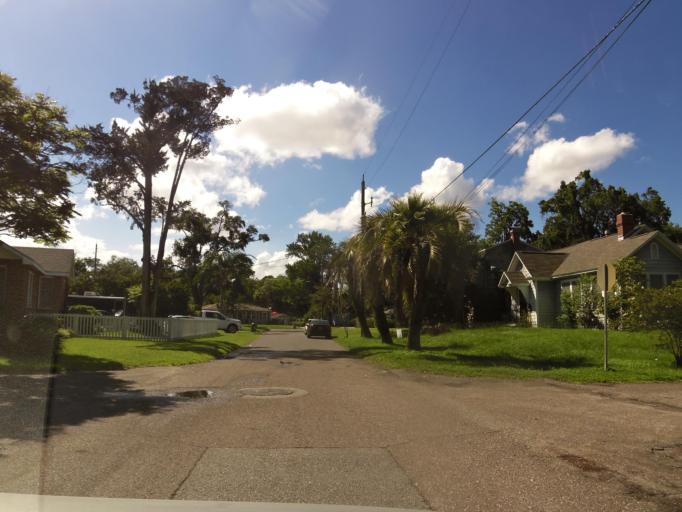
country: US
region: Florida
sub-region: Duval County
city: Jacksonville
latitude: 30.2992
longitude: -81.7161
